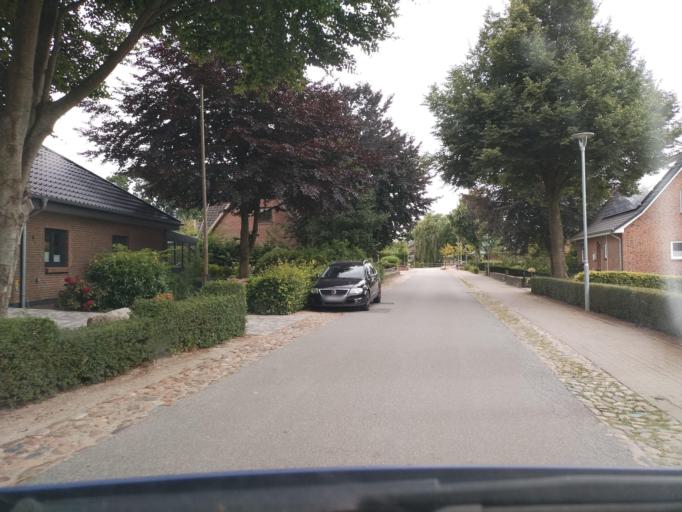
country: DE
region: Schleswig-Holstein
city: Husby
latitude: 54.4982
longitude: 9.4855
